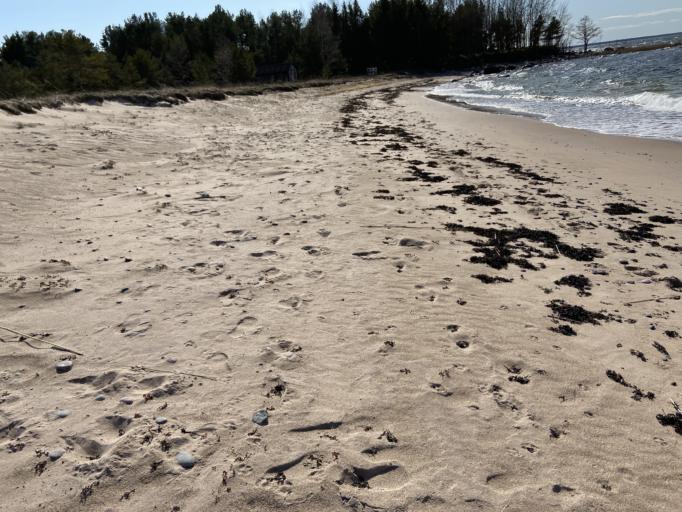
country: EE
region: Harju
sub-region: Loksa linn
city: Loksa
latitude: 59.6577
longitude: 25.6760
